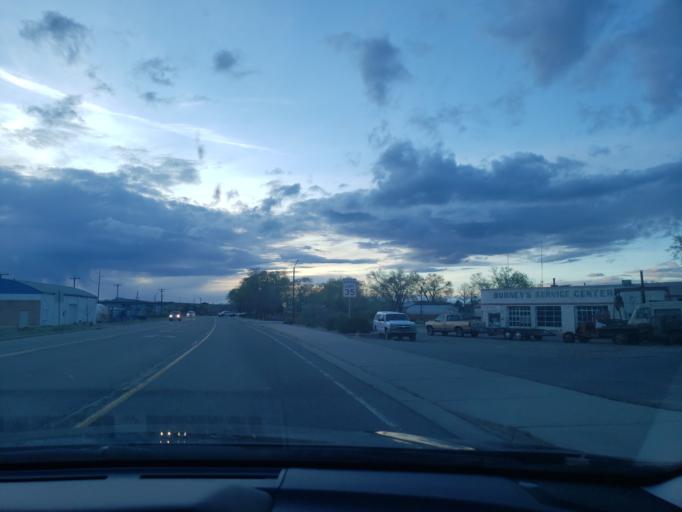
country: US
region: Colorado
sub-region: Mesa County
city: Fruita
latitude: 39.1555
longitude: -108.7318
